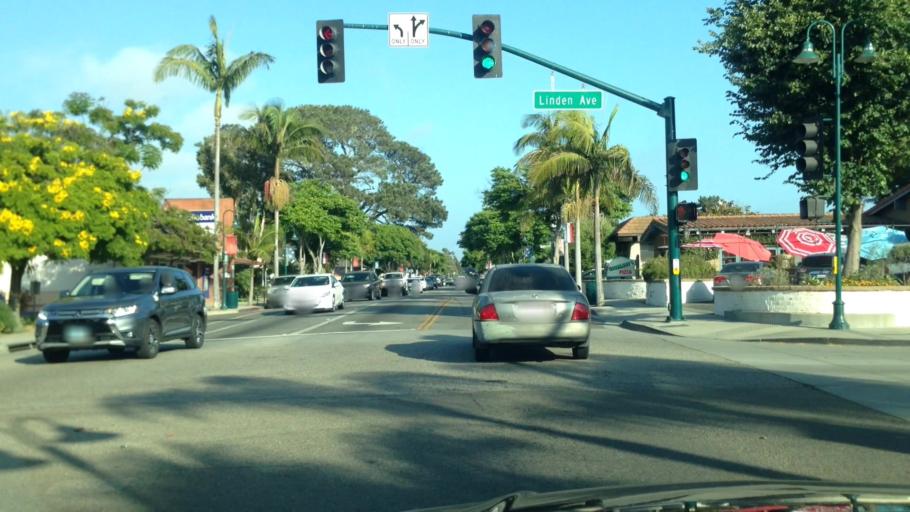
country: US
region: California
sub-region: Santa Barbara County
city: Carpinteria
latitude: 34.3990
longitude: -119.5185
